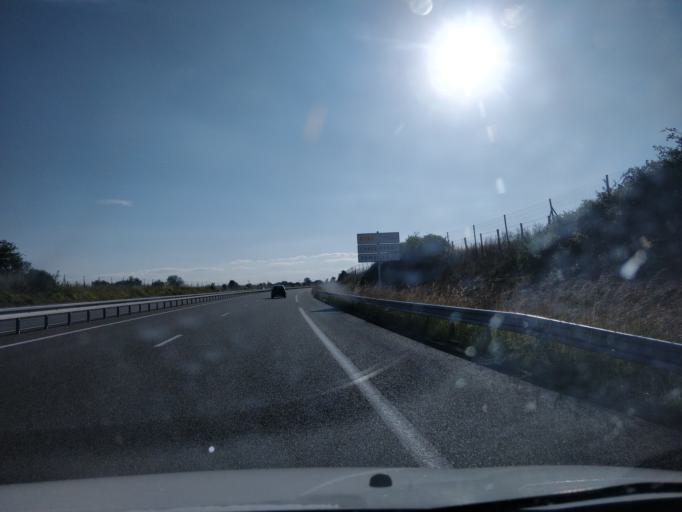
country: FR
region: Pays de la Loire
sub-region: Departement de Maine-et-Loire
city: Combree
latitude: 47.7288
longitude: -1.0922
